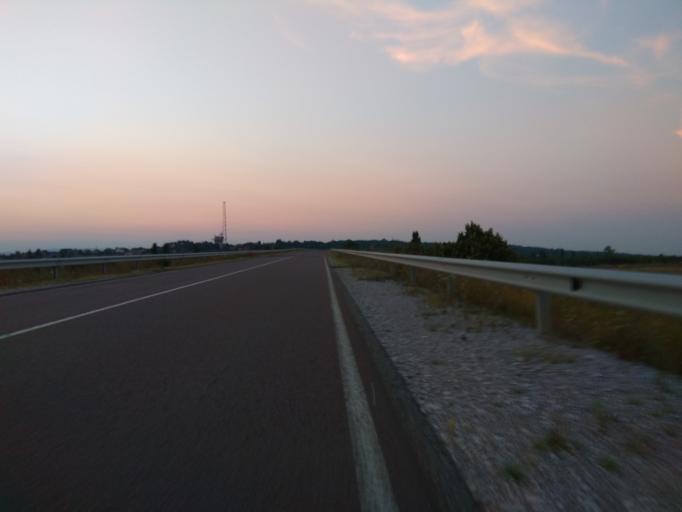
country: HU
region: Borsod-Abauj-Zemplen
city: Emod
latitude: 47.9331
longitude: 20.8292
